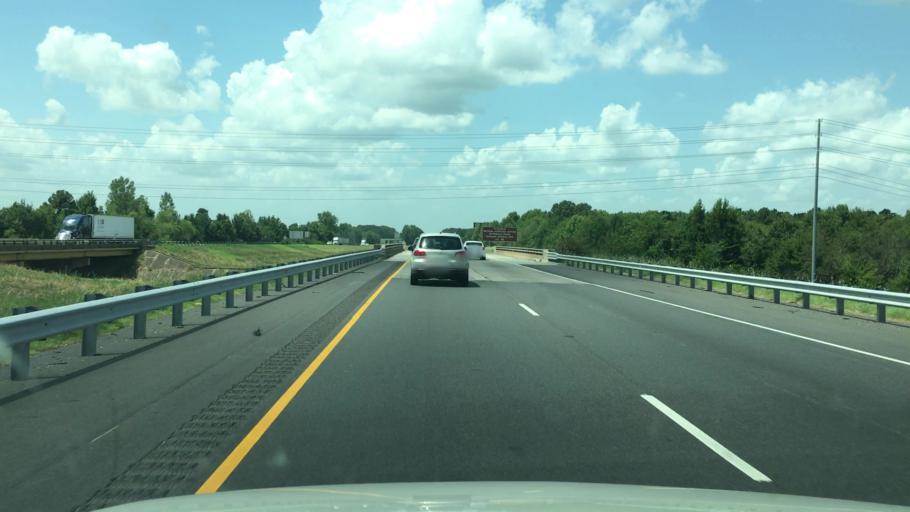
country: US
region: Arkansas
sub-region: Hempstead County
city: Hope
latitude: 33.6898
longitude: -93.6000
